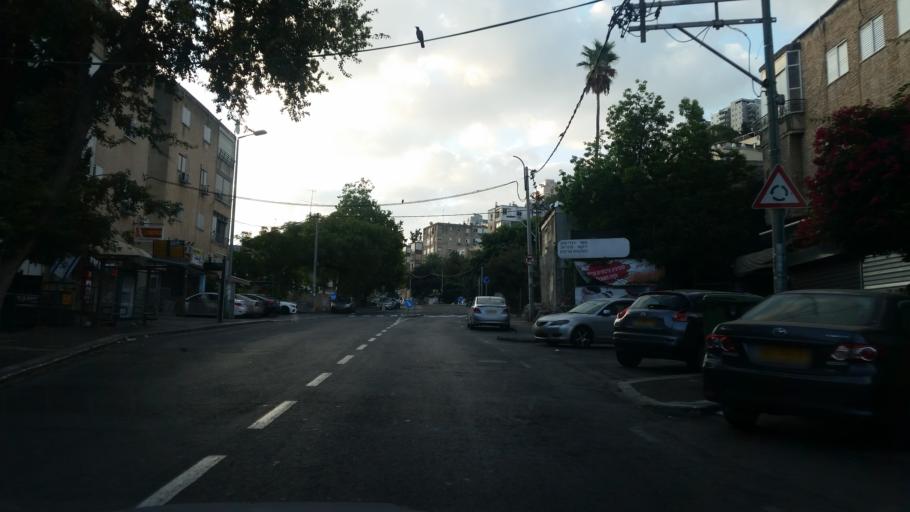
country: IL
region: Haifa
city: Haifa
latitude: 32.8004
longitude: 35.0117
